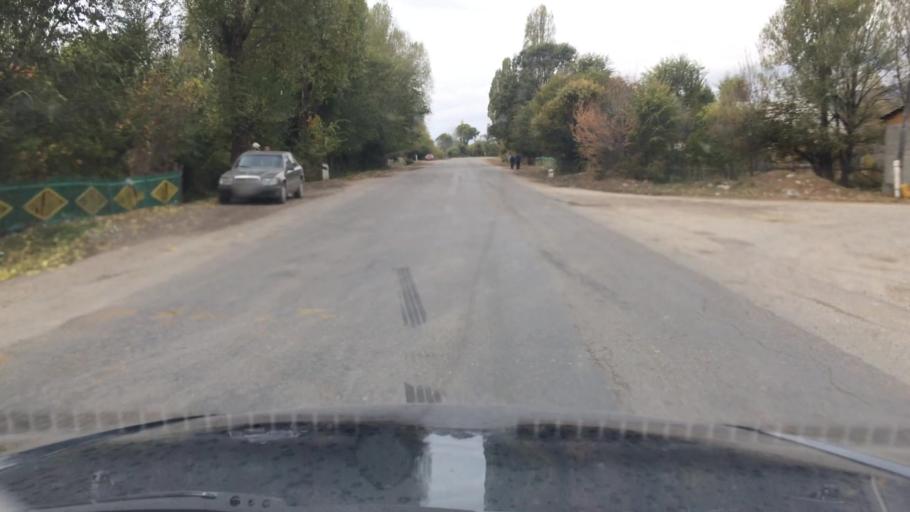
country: KG
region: Ysyk-Koel
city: Pokrovka
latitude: 42.7371
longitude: 77.9355
